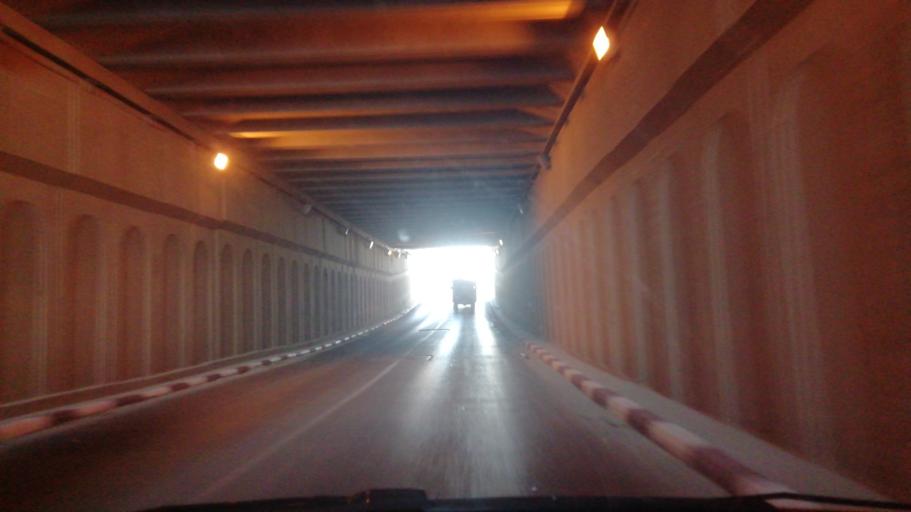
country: DZ
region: Mascara
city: Mascara
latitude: 35.5903
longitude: 0.0605
